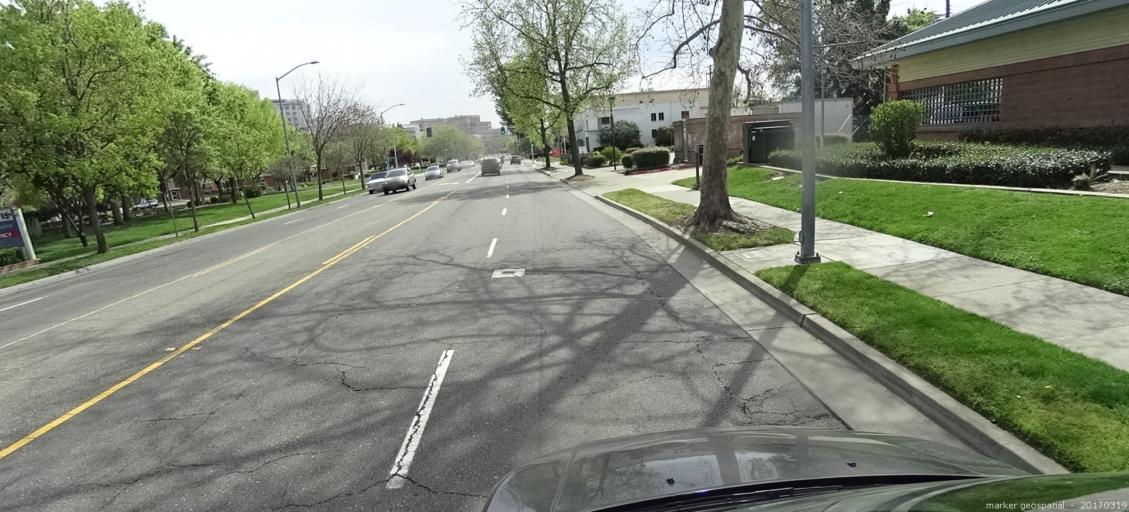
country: US
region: California
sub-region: Sacramento County
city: Sacramento
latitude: 38.5573
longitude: -121.4605
